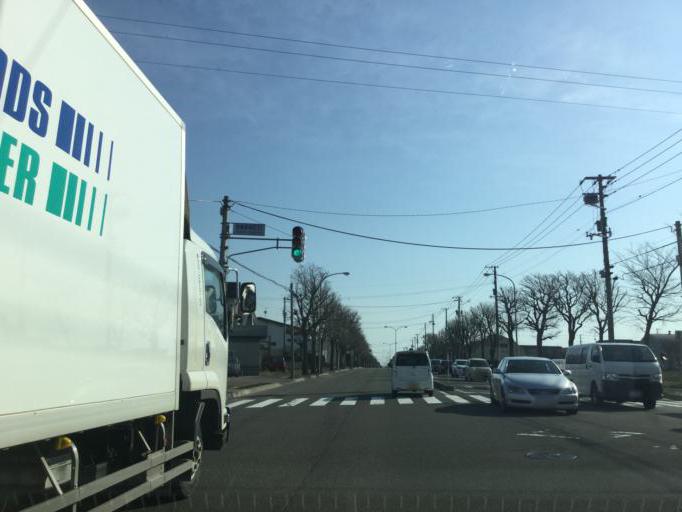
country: JP
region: Hokkaido
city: Ebetsu
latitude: 43.0911
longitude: 141.5078
